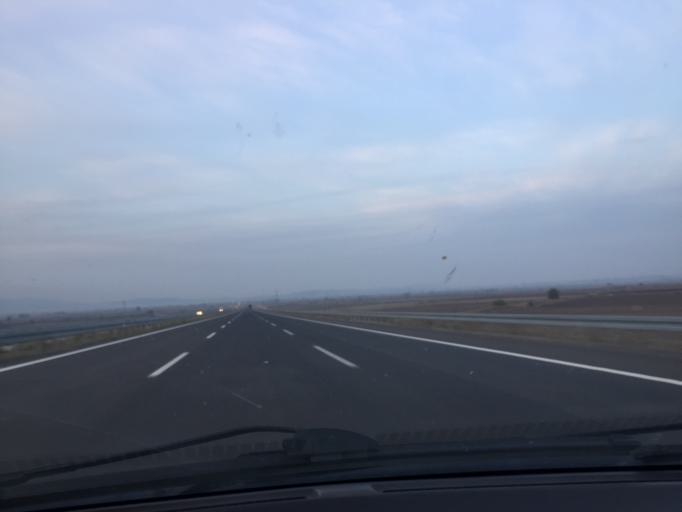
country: TR
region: Manisa
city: Halitpasa
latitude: 38.7072
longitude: 27.6458
